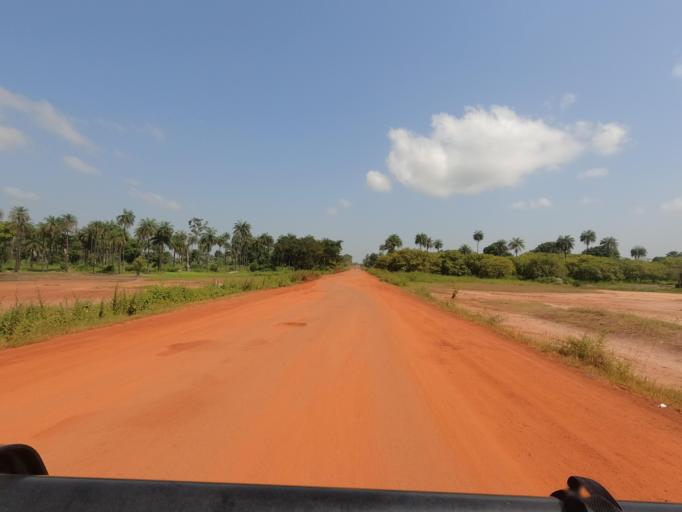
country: GW
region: Cacheu
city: Canchungo
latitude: 12.2766
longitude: -15.7866
